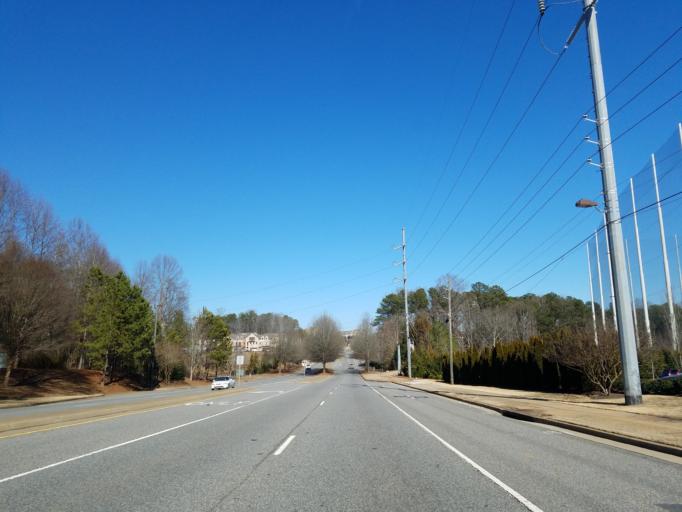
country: US
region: Georgia
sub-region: Fulton County
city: Alpharetta
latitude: 34.0455
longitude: -84.3088
